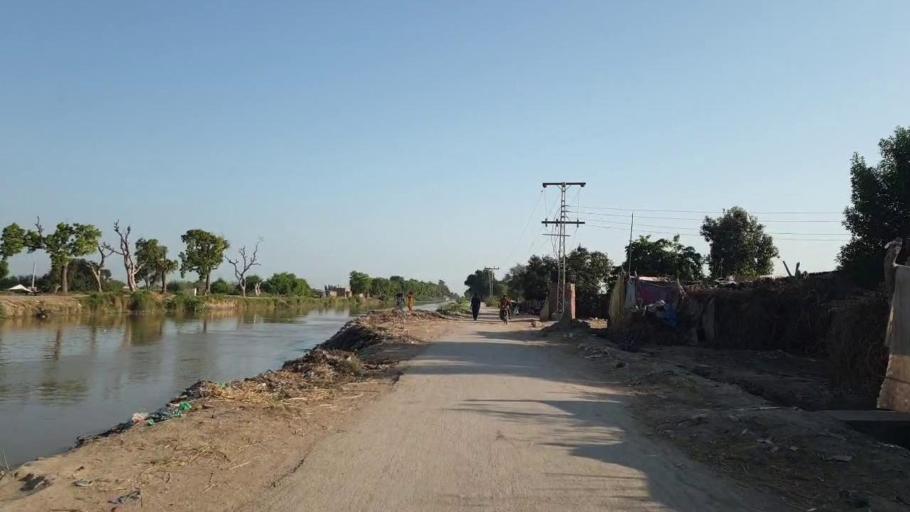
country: PK
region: Sindh
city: Hyderabad
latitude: 25.3226
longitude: 68.4270
